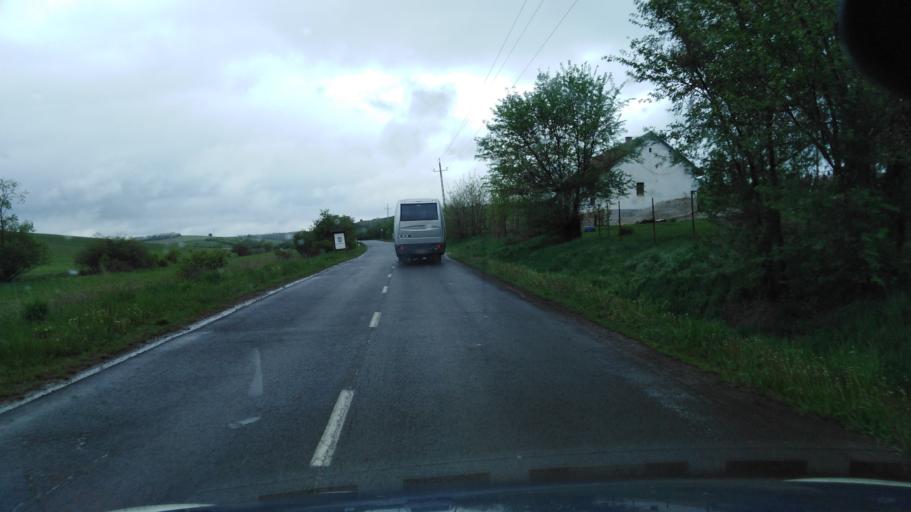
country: HU
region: Nograd
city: Rimoc
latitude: 47.9995
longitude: 19.6189
